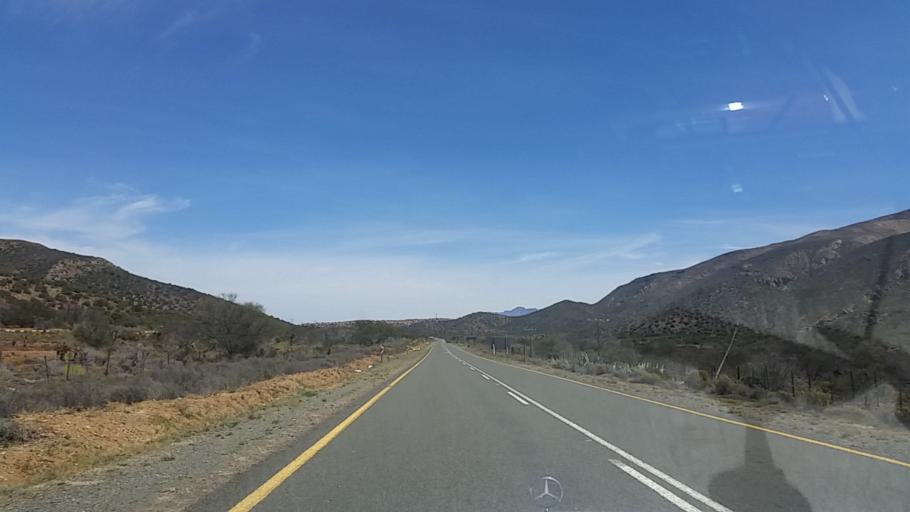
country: ZA
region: Eastern Cape
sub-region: Cacadu District Municipality
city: Willowmore
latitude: -33.4095
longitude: 23.3329
